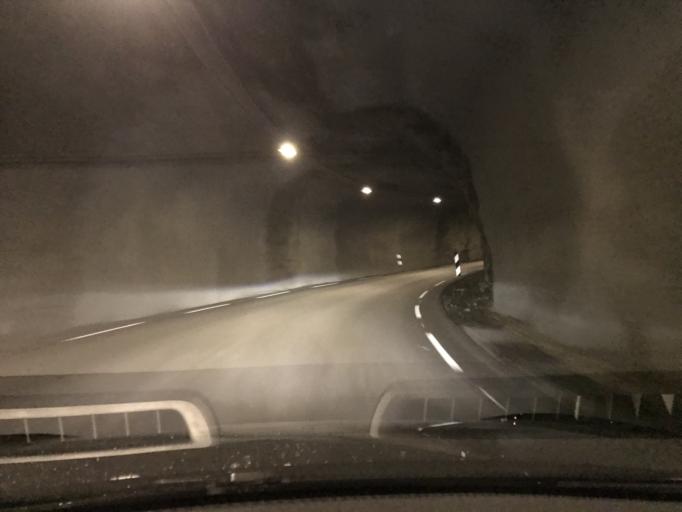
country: NO
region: Sogn og Fjordane
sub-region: Aurland
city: Aurlandsvangen
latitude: 60.8599
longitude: 7.3109
